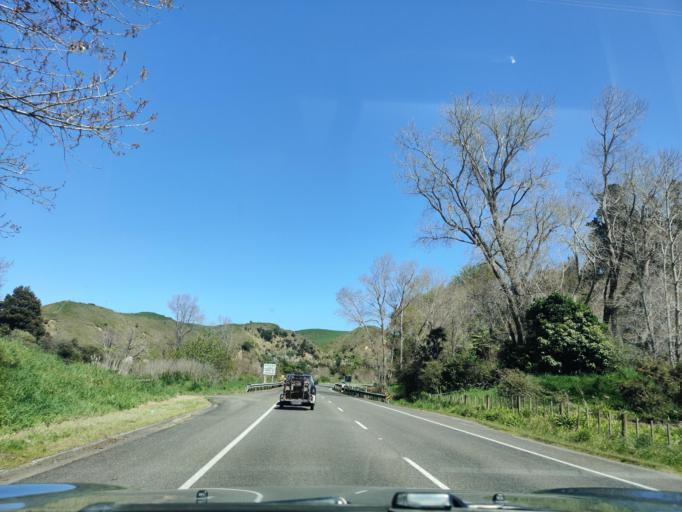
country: NZ
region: Manawatu-Wanganui
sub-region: Wanganui District
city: Wanganui
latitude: -39.8314
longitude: 174.8903
